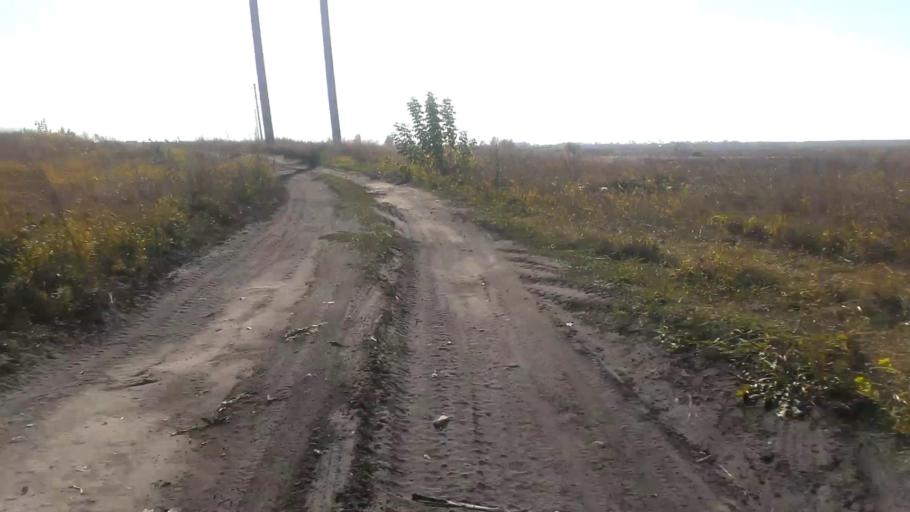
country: RU
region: Altai Krai
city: Novoaltaysk
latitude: 53.3661
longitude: 83.9453
